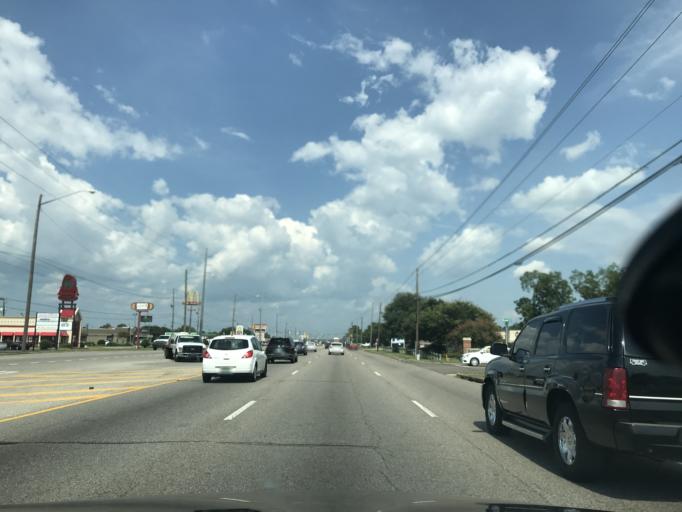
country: US
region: Alabama
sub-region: Montgomery County
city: Montgomery
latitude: 32.3820
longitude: -86.2022
